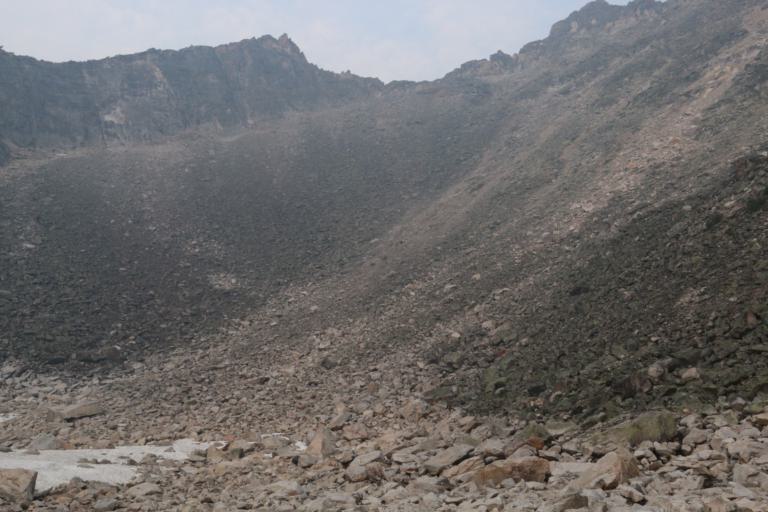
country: RU
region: Respublika Buryatiya
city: Kichera
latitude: 56.2412
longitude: 110.7076
